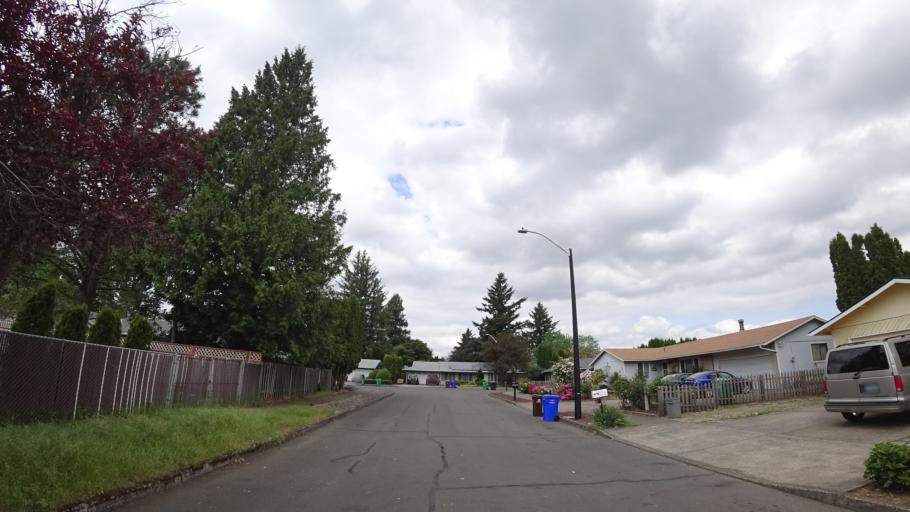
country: US
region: Oregon
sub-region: Multnomah County
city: Gresham
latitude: 45.5093
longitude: -122.4710
